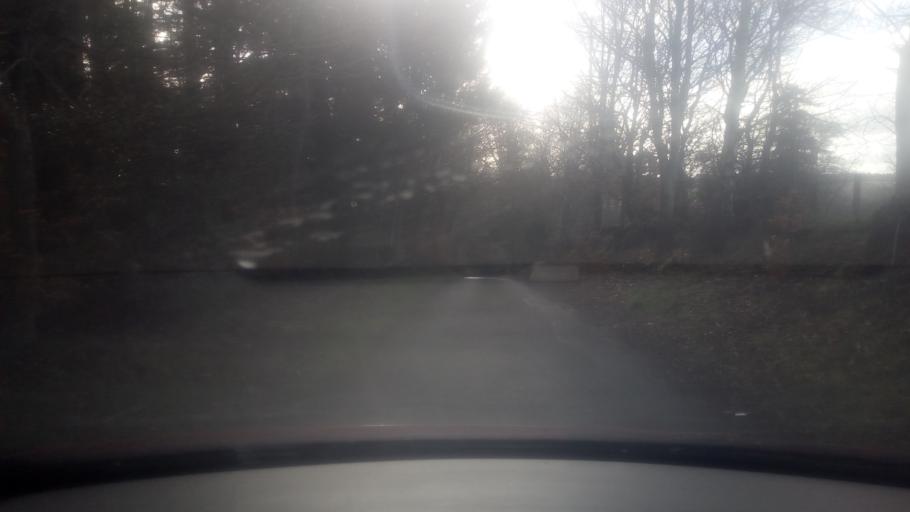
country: GB
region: Scotland
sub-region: The Scottish Borders
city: Jedburgh
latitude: 55.5165
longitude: -2.5692
